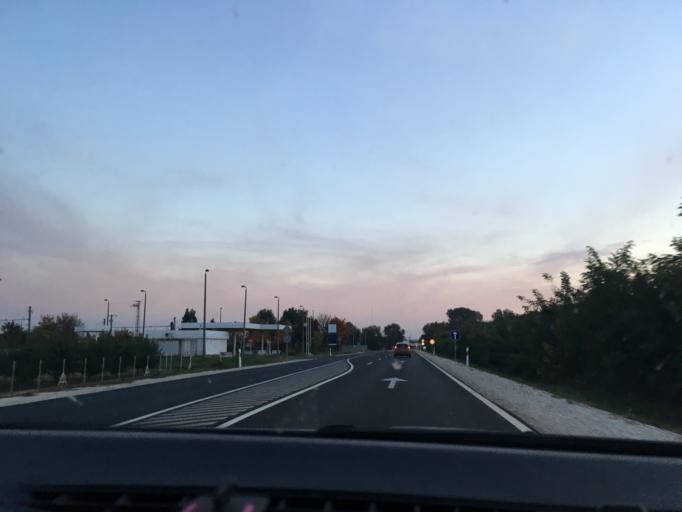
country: HU
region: Hajdu-Bihar
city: Debrecen
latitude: 47.5877
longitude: 21.6546
